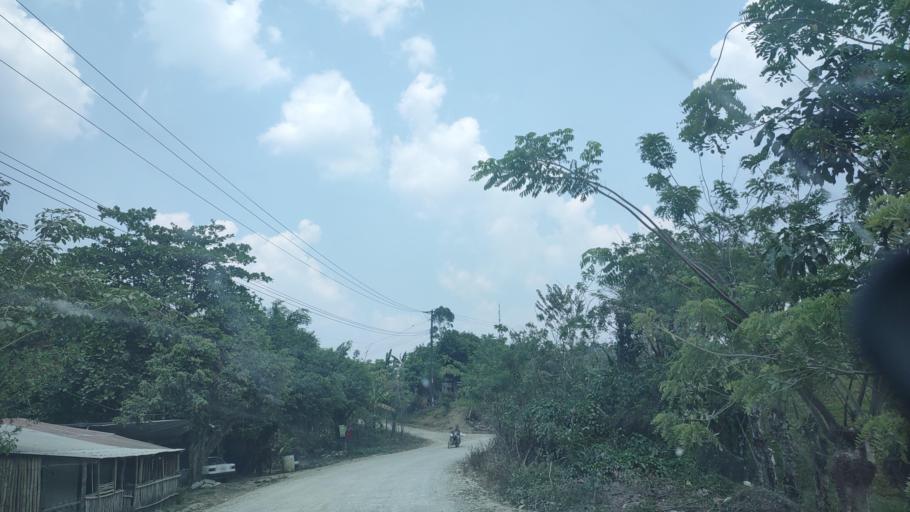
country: MX
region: Tabasco
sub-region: Huimanguillo
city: Francisco Rueda
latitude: 17.6022
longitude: -93.9020
